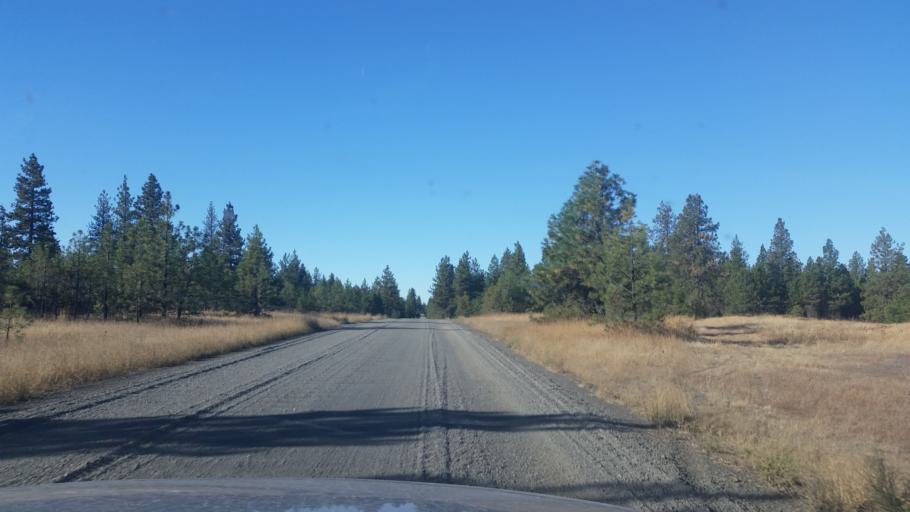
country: US
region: Washington
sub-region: Spokane County
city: Medical Lake
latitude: 47.4317
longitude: -117.7837
